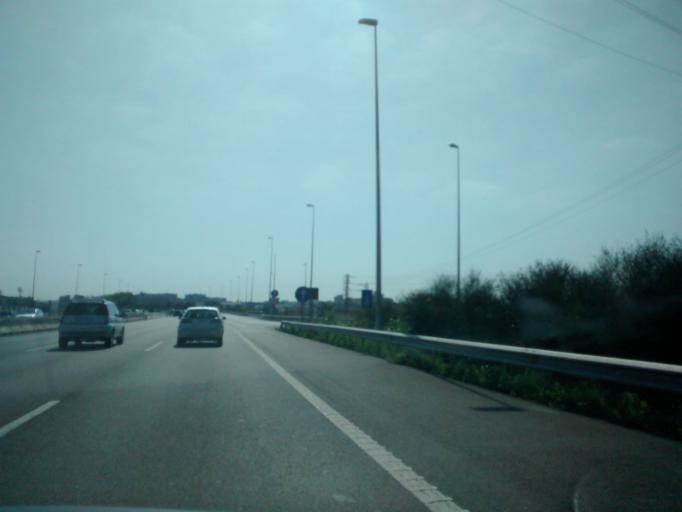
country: ES
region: Catalonia
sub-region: Provincia de Barcelona
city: Sant Feliu de Llobregat
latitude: 41.3728
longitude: 2.0460
